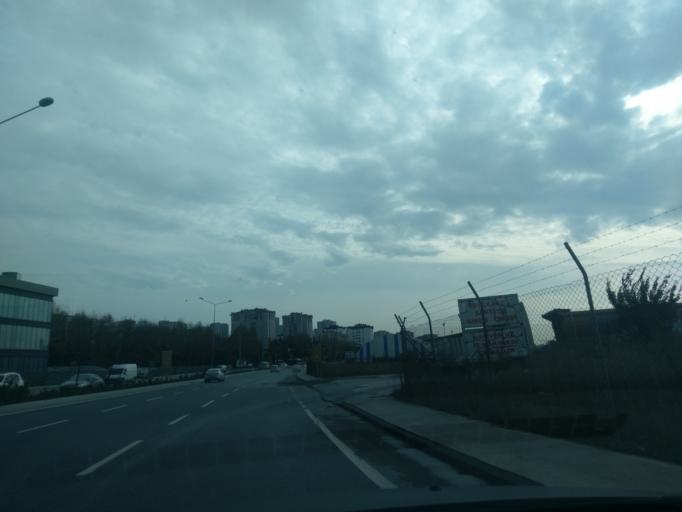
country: TR
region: Istanbul
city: Basaksehir
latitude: 41.0599
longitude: 28.7734
